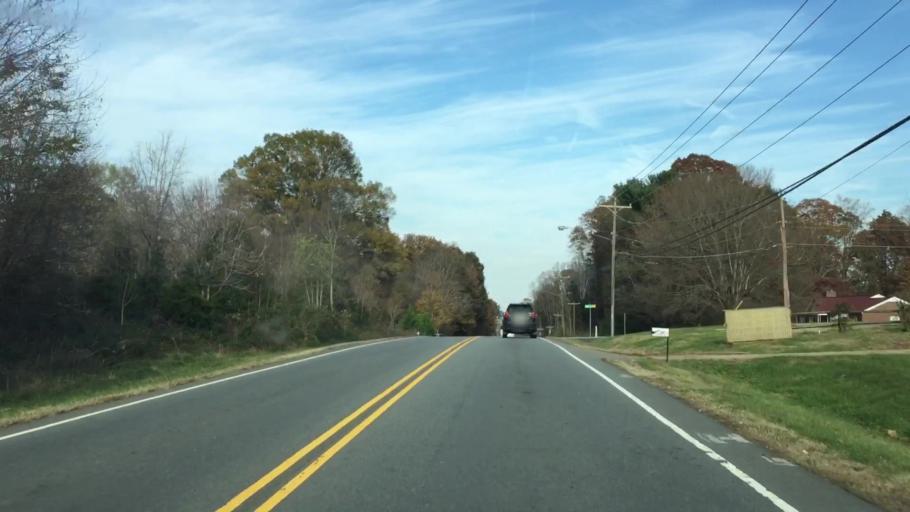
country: US
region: North Carolina
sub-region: Forsyth County
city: Walkertown
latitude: 36.1308
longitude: -80.1717
